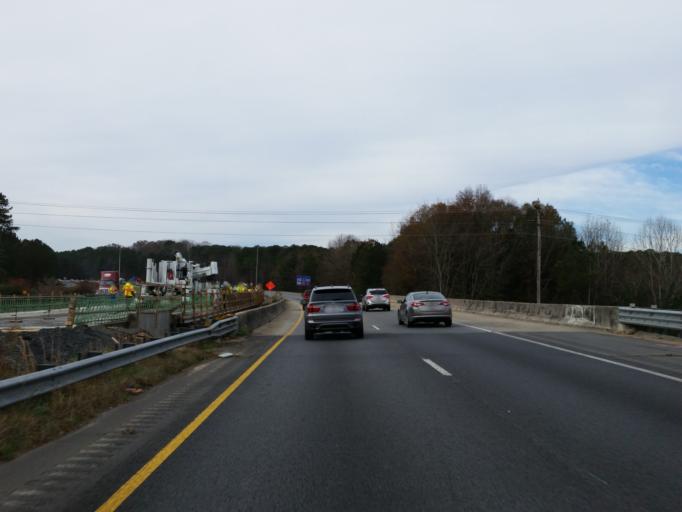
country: US
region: Georgia
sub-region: Cherokee County
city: Woodstock
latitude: 34.0525
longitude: -84.5554
